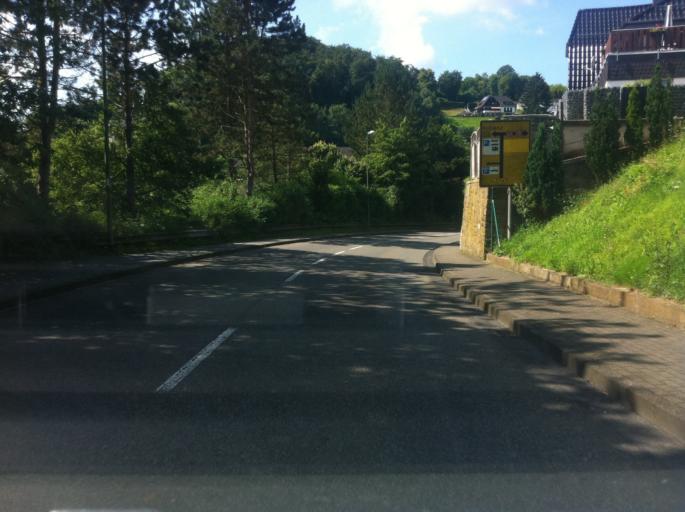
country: DE
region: North Rhine-Westphalia
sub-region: Regierungsbezirk Koln
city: Blankenheim
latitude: 50.4376
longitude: 6.6533
